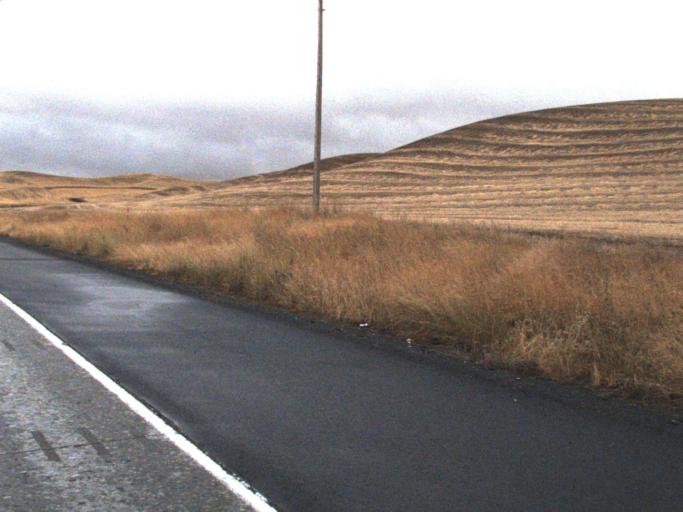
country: US
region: Washington
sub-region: Whitman County
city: Colfax
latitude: 47.0433
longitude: -117.3758
